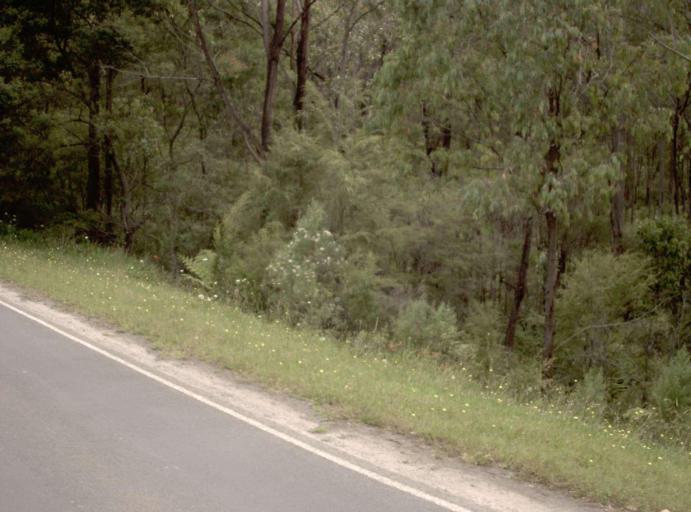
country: AU
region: Victoria
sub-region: Latrobe
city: Traralgon
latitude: -38.0998
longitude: 146.4423
